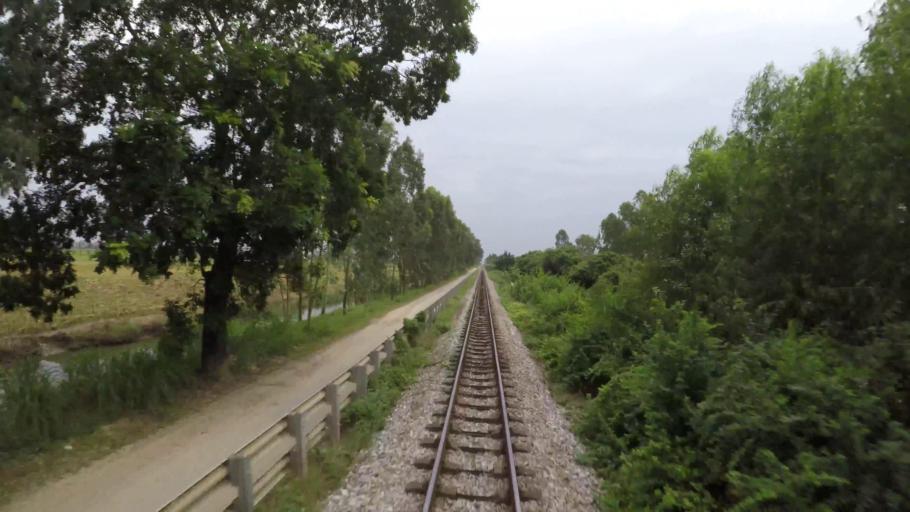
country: VN
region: Hai Duong
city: Lai Cach
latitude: 20.9551
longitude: 106.2169
